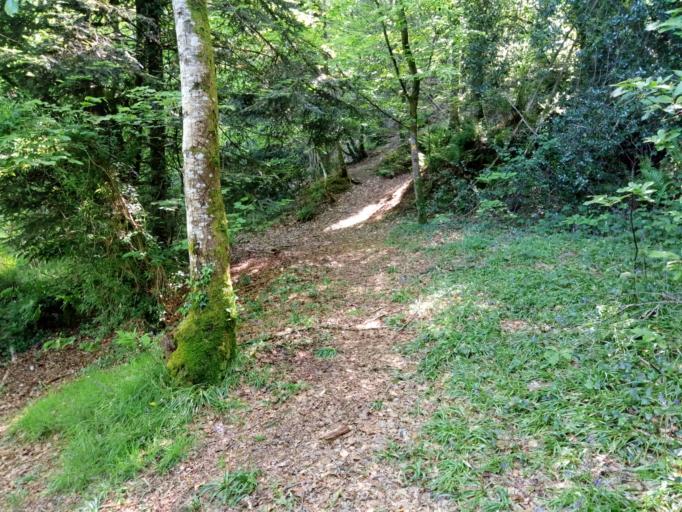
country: FR
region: Brittany
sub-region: Departement du Finistere
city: Chateaulin
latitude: 48.1976
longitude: -4.0724
